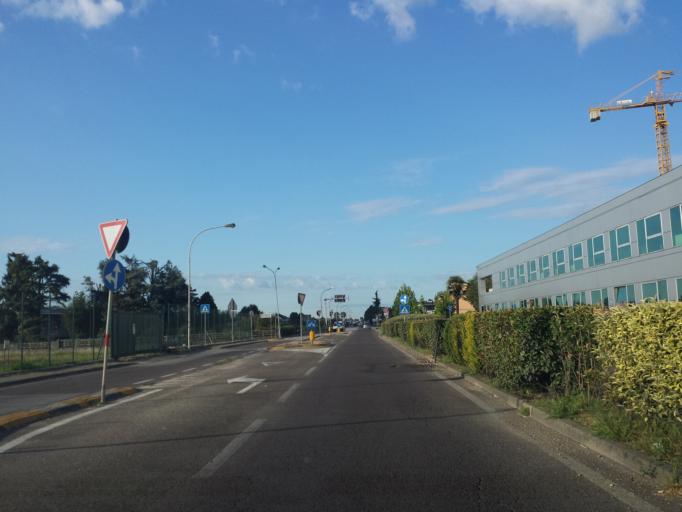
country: IT
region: Veneto
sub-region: Provincia di Vicenza
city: Brendola
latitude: 45.4924
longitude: 11.4287
